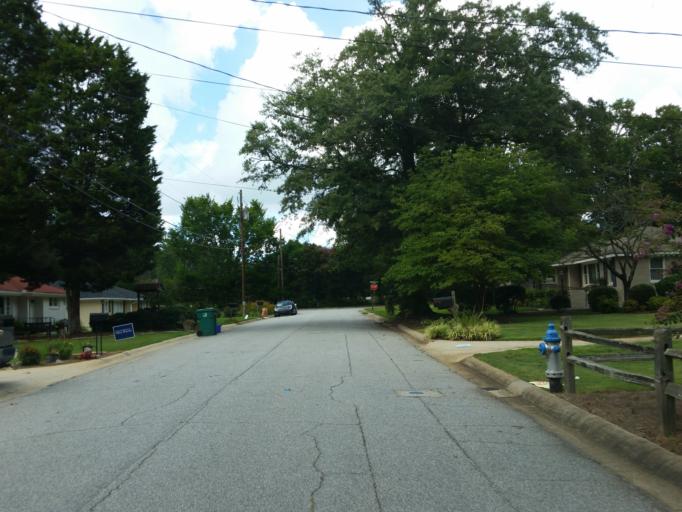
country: US
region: Georgia
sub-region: Cobb County
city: Smyrna
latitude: 33.8740
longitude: -84.5217
